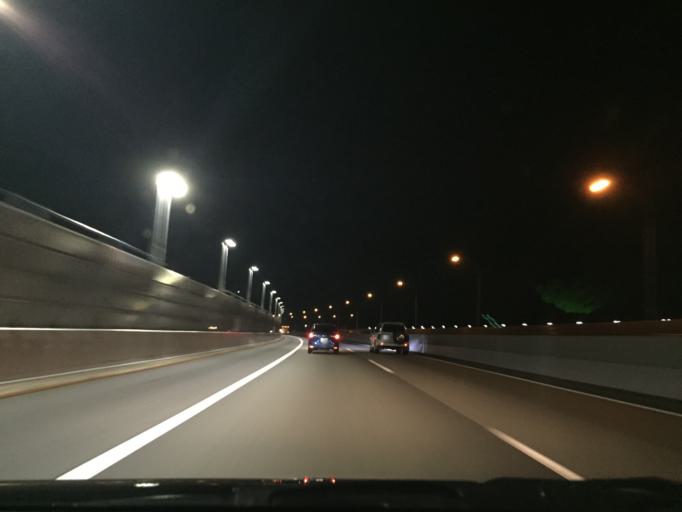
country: JP
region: Kanagawa
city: Hadano
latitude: 35.3474
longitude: 139.1510
